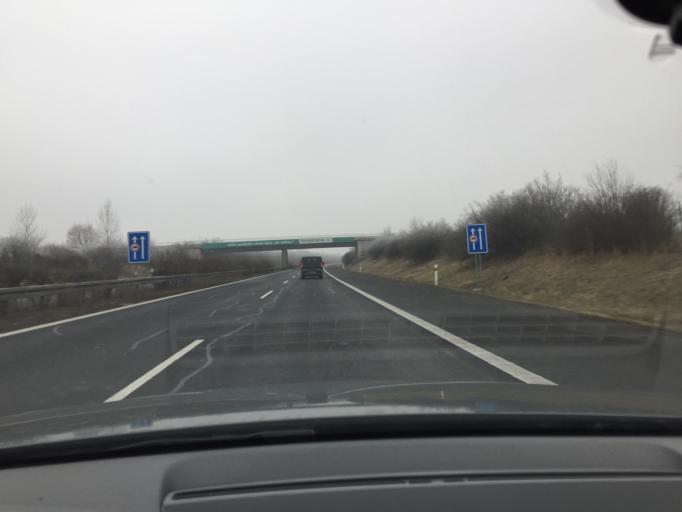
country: CZ
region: Ustecky
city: Budyne nad Ohri
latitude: 50.4431
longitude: 14.1452
